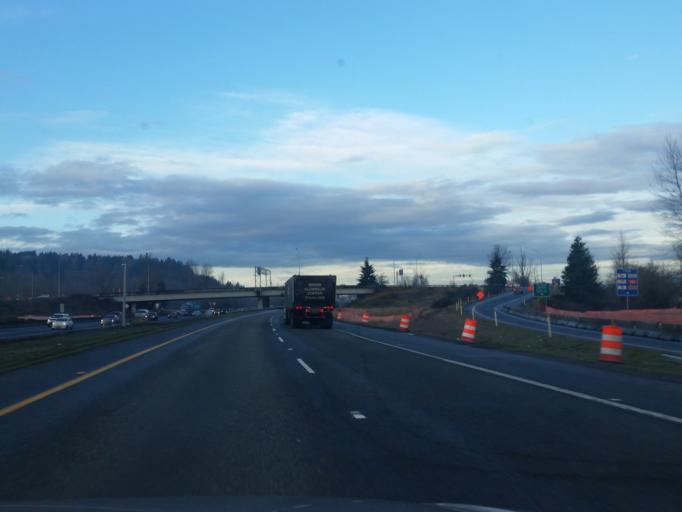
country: US
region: Washington
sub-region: King County
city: Algona
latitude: 47.2930
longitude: -122.2577
